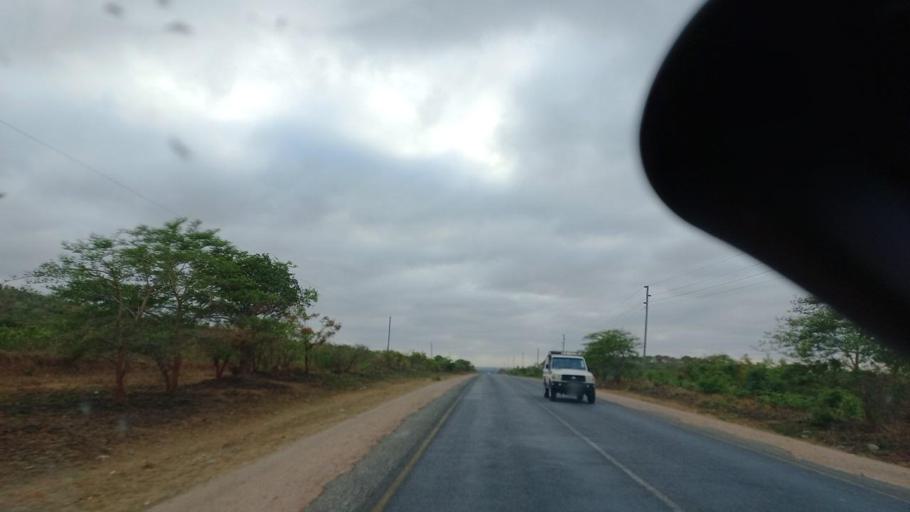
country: ZM
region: Lusaka
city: Chongwe
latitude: -15.3418
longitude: 28.5994
